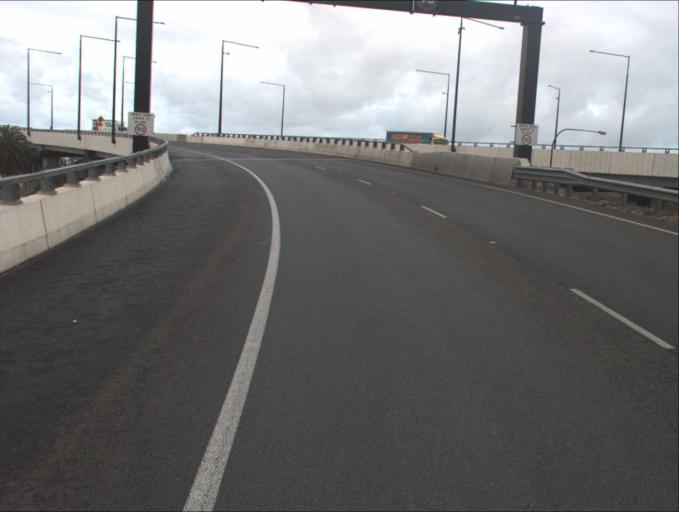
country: AU
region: South Australia
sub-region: Port Adelaide Enfield
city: Blair Athol
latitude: -34.8337
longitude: 138.5635
